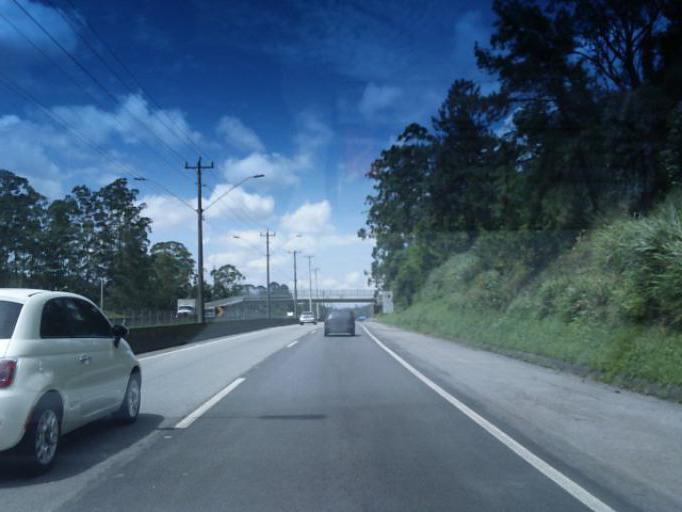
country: BR
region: Sao Paulo
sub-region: Itapecerica Da Serra
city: Itapecerica da Serra
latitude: -23.7590
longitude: -46.9034
